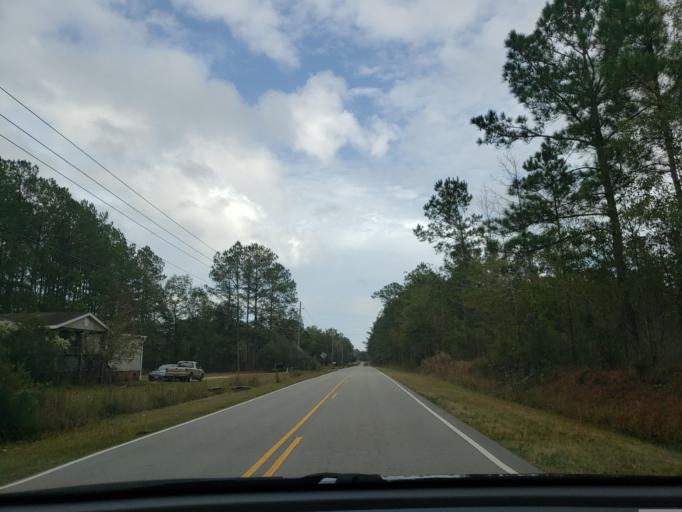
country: US
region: North Carolina
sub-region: Onslow County
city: Jacksonville
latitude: 34.7013
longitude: -77.5690
